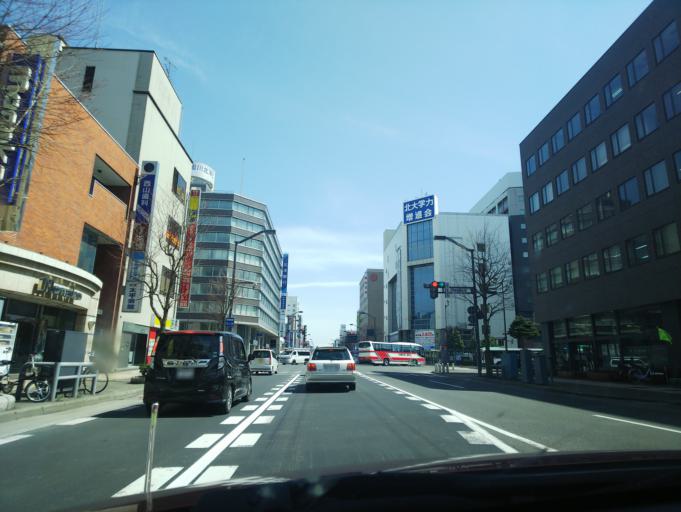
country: JP
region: Hokkaido
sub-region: Asahikawa-shi
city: Asahikawa
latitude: 43.7687
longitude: 142.3617
